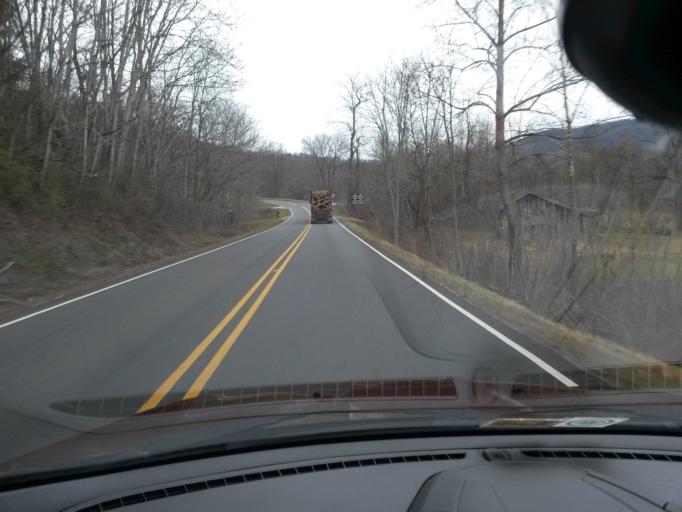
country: US
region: Virginia
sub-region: City of Buena Vista
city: Buena Vista
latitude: 37.6892
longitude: -79.2401
